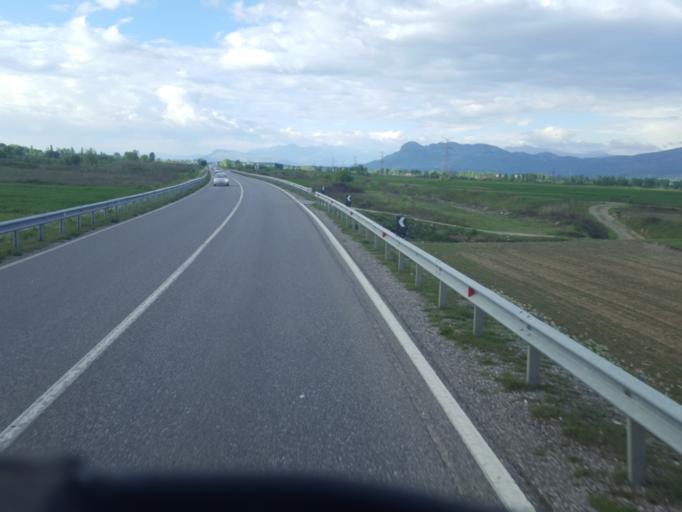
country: AL
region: Lezhe
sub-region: Rrethi i Lezhes
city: Balldreni i Ri
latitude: 41.8417
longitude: 19.6439
